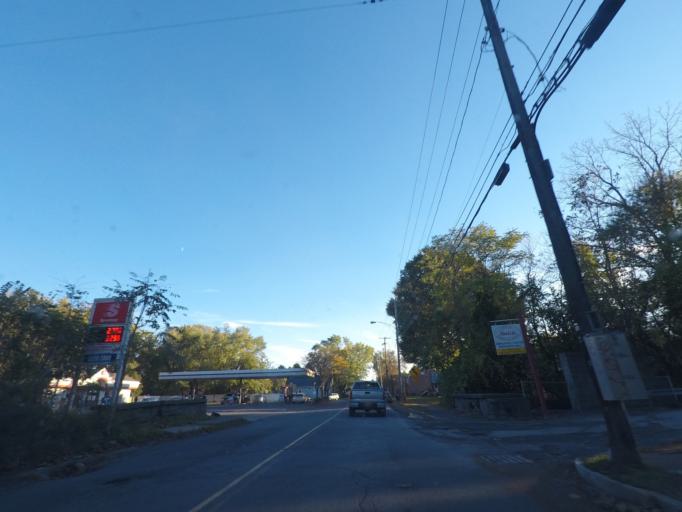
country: US
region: New York
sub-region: Albany County
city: Green Island
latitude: 42.7546
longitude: -73.7006
